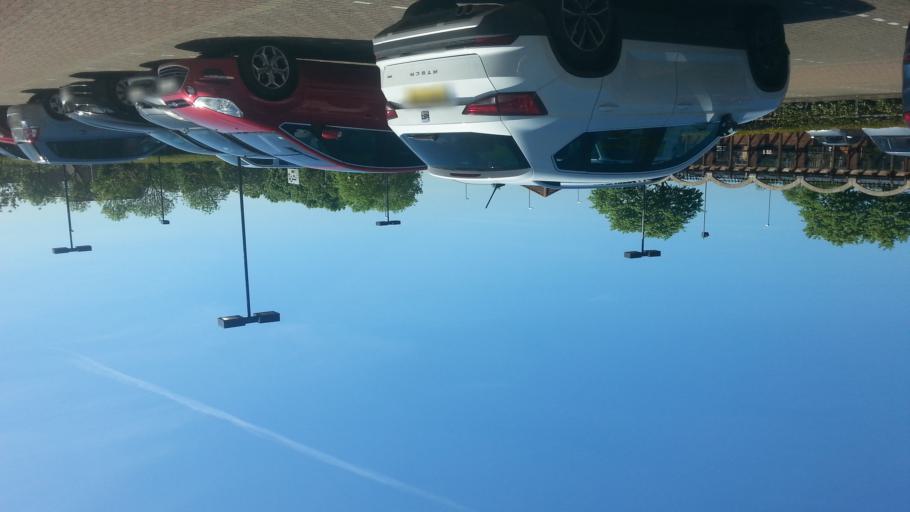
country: GB
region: England
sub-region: Cambridgeshire
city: Huntingdon
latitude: 52.3526
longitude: -0.1831
